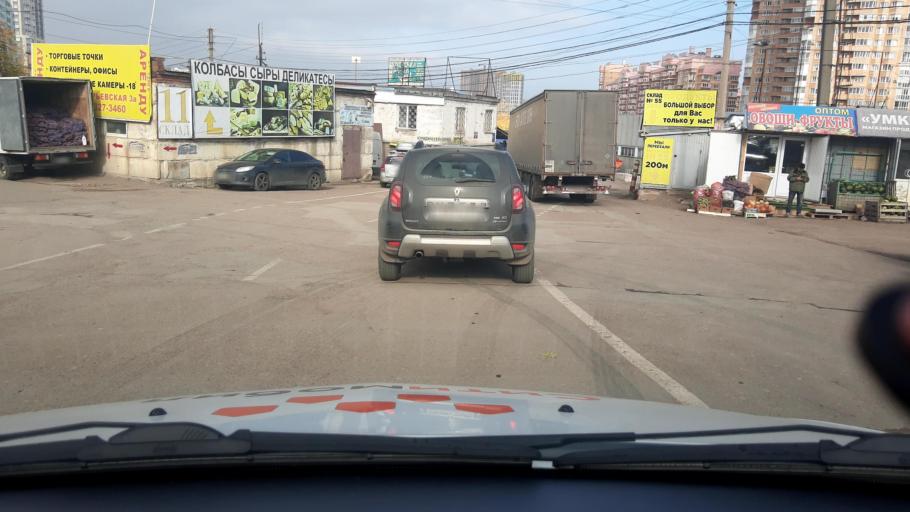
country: RU
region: Bashkortostan
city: Ufa
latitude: 54.7144
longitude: 55.9866
